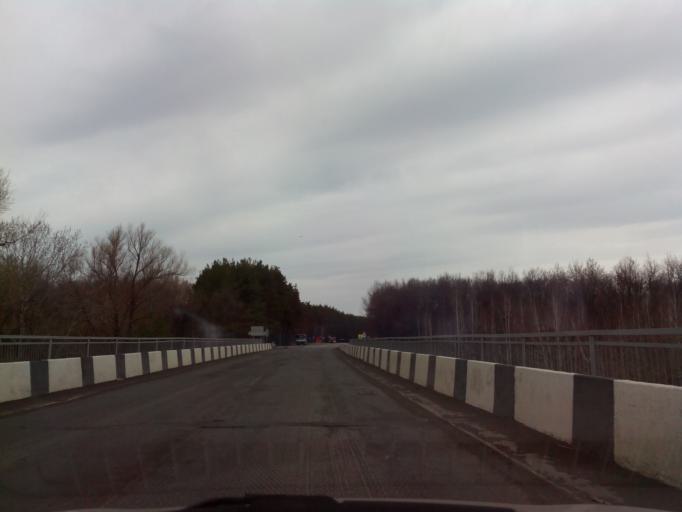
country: RU
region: Tambov
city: Znamenka
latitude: 52.5316
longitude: 41.3568
